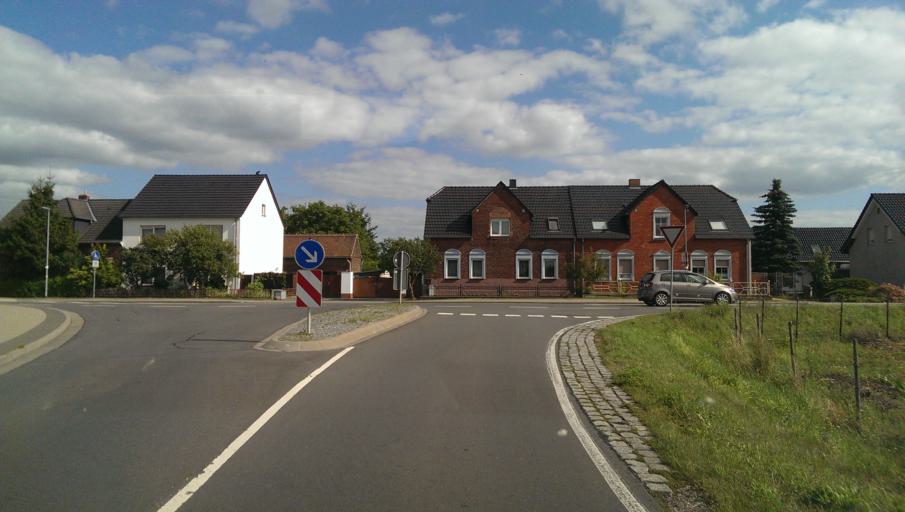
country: DE
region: Saxony-Anhalt
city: Radis
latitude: 51.7505
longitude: 12.5109
